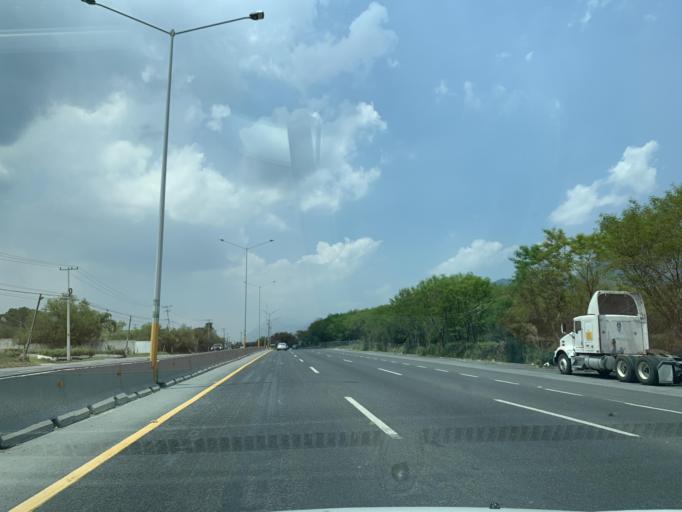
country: MX
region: Nuevo Leon
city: Santiago
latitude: 25.4850
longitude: -100.1820
